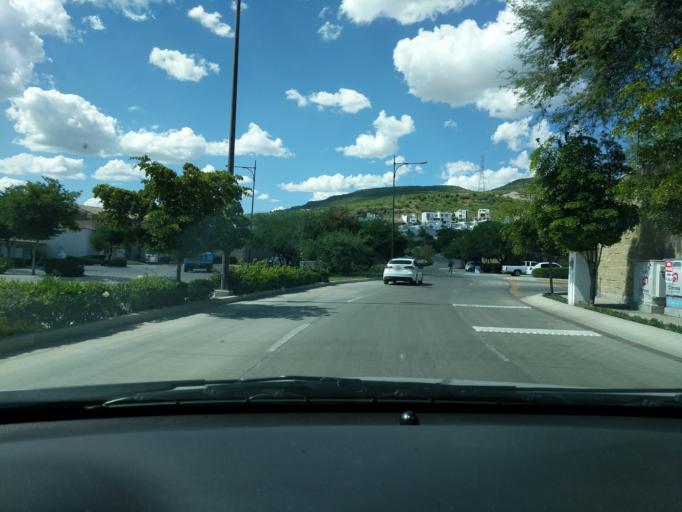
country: MX
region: Guanajuato
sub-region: Leon
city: Medina
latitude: 21.1328
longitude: -101.6046
